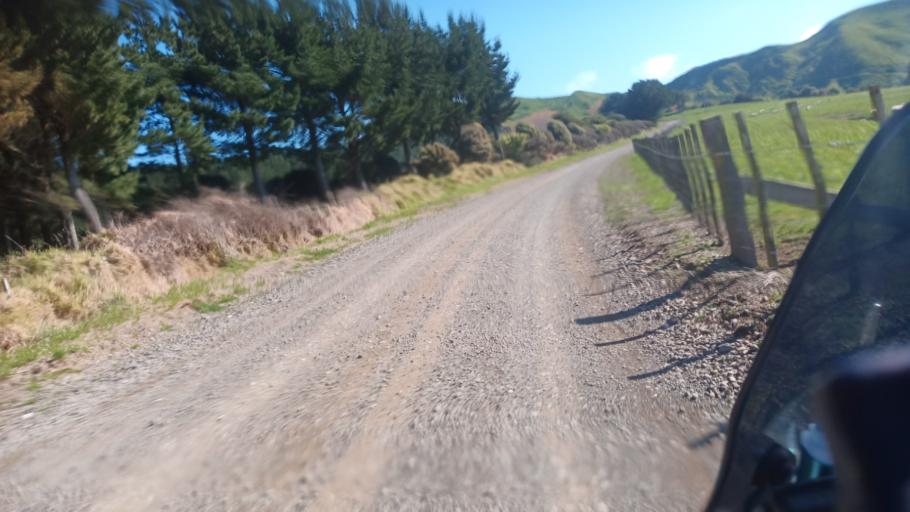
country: NZ
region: Gisborne
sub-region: Gisborne District
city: Gisborne
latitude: -39.1542
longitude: 177.9165
